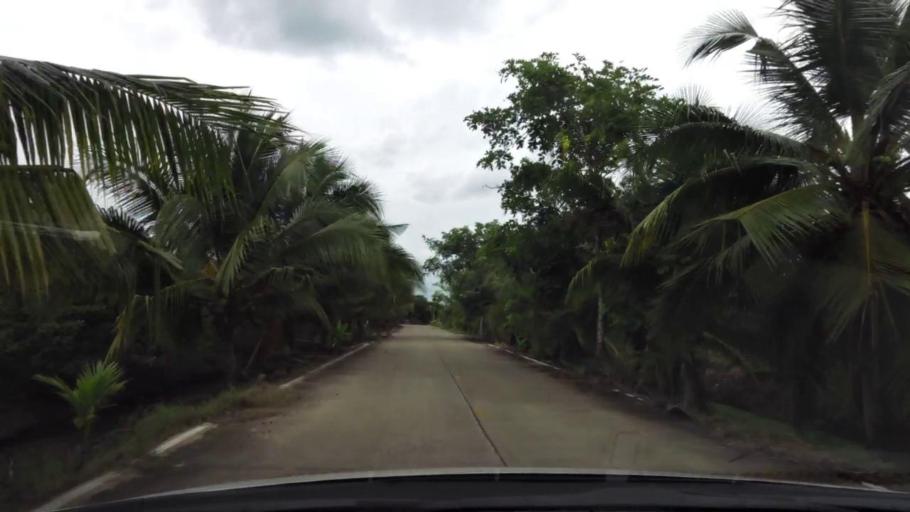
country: TH
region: Ratchaburi
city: Damnoen Saduak
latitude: 13.5541
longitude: 100.0197
